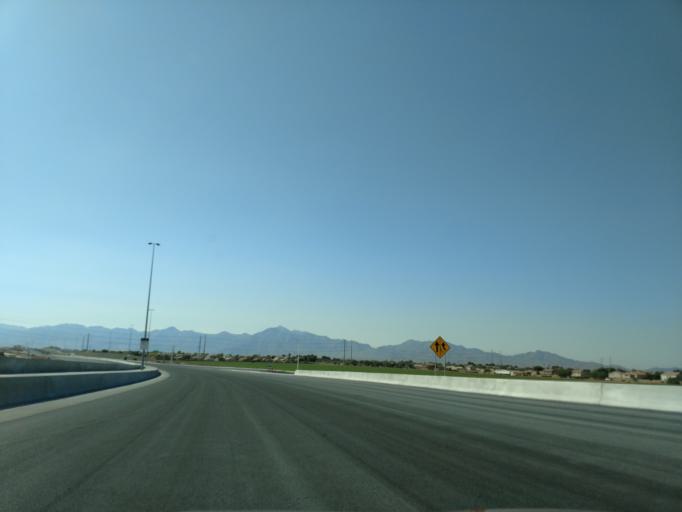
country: US
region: Arizona
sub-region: Maricopa County
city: Laveen
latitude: 33.4209
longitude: -112.1908
